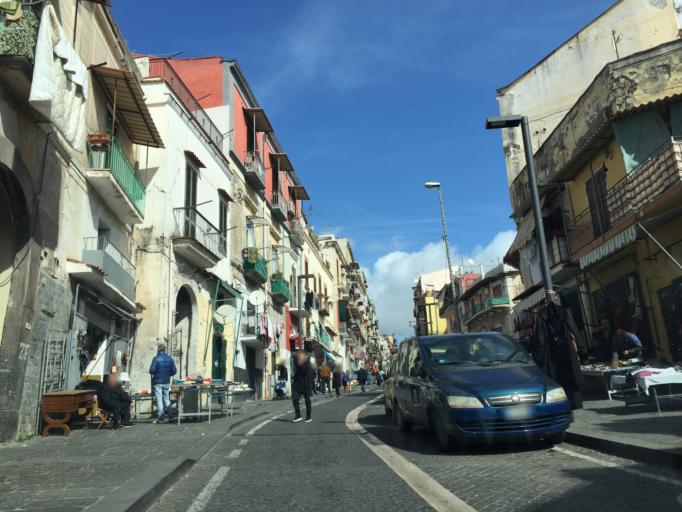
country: IT
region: Campania
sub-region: Provincia di Napoli
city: Portici
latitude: 40.8087
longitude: 14.3490
